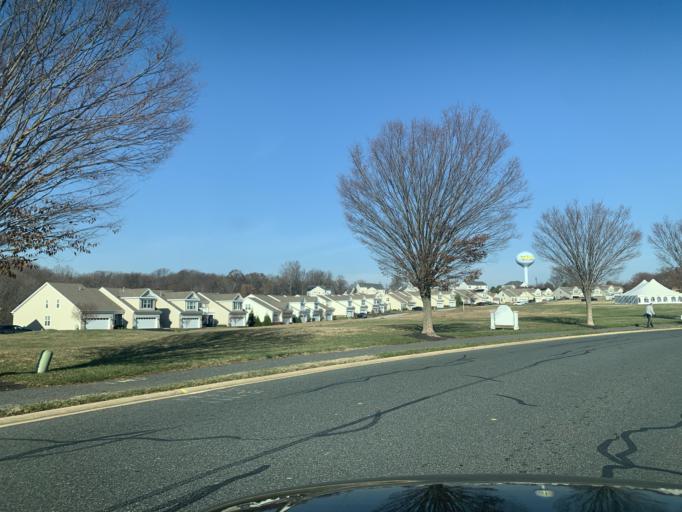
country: US
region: Maryland
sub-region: Harford County
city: Havre de Grace
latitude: 39.5516
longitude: -76.1286
